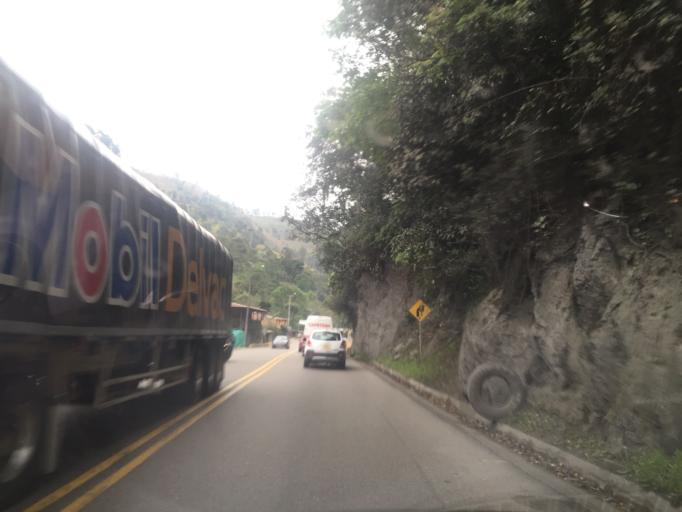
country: CO
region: Tolima
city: Cajamarca
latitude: 4.4337
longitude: -75.4533
